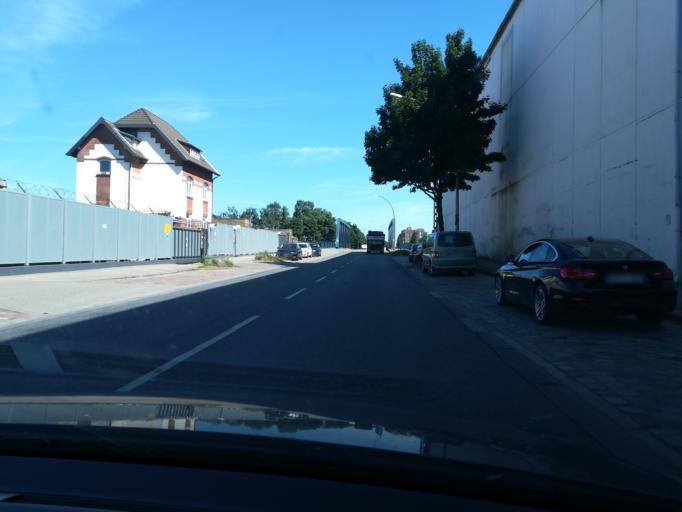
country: DE
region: Hamburg
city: Rothenburgsort
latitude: 53.5265
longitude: 10.0284
